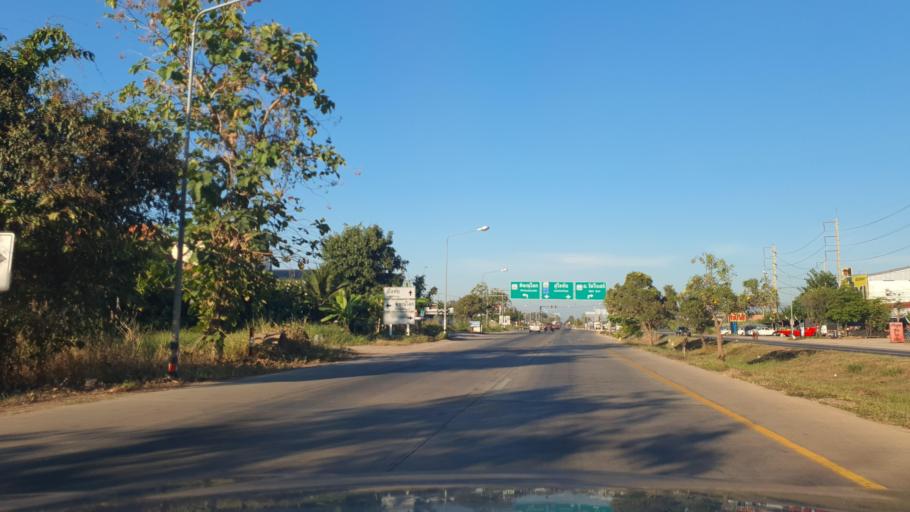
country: TH
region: Phitsanulok
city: Phitsanulok
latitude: 16.8647
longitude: 100.2520
